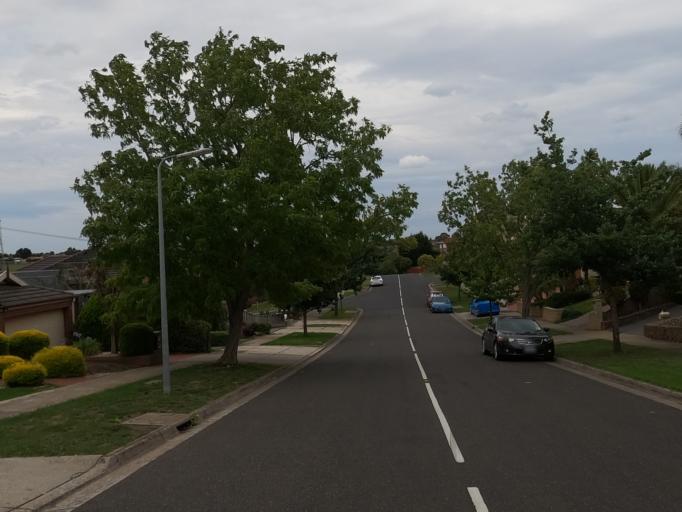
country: AU
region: Victoria
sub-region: Hume
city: Meadow Heights
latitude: -37.6489
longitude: 144.9036
